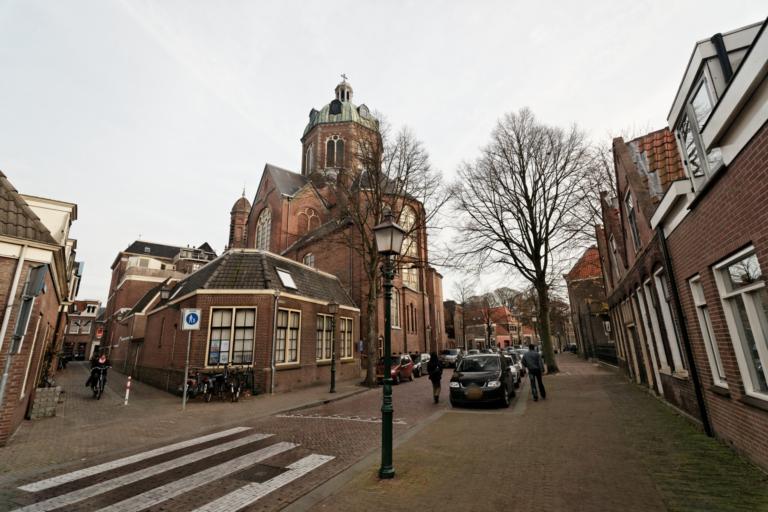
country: NL
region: North Holland
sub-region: Gemeente Hoorn
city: Hoorn
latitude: 52.6399
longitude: 5.0570
